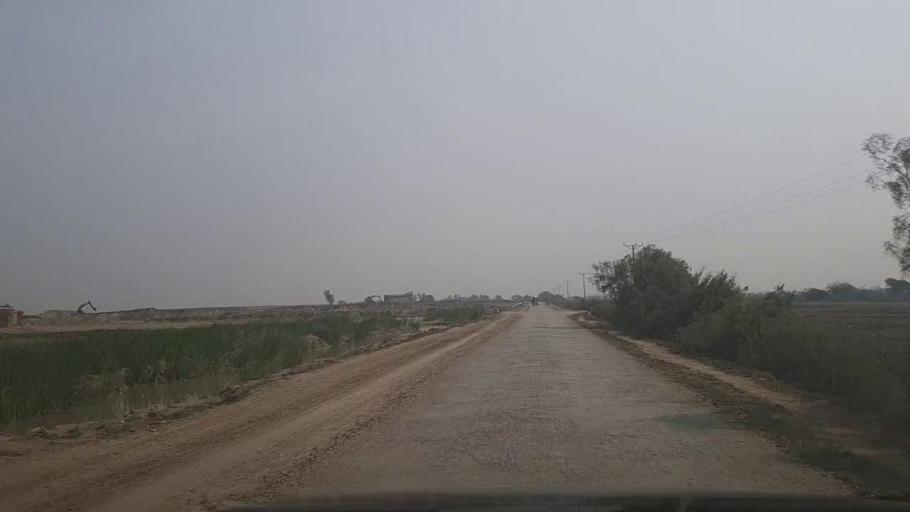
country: PK
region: Sindh
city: Mirpur Sakro
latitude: 24.4755
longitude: 67.6656
